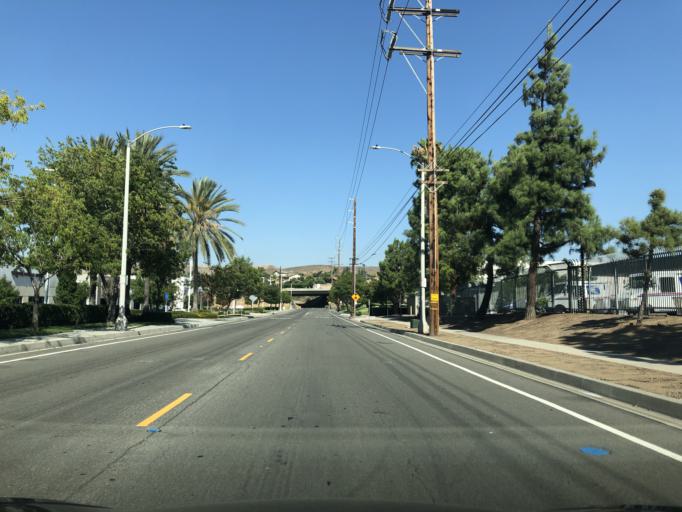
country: US
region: California
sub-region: Riverside County
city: El Cerrito
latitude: 33.8539
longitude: -117.5386
